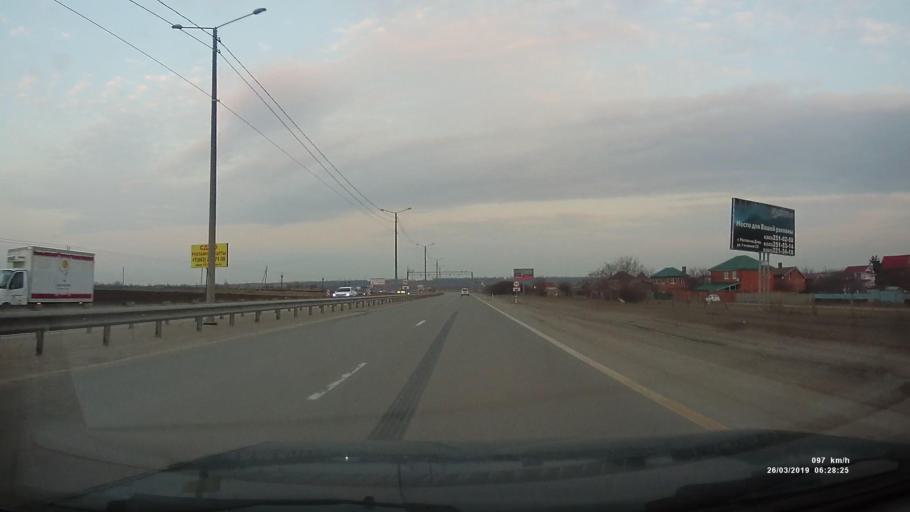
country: RU
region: Rostov
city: Krym
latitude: 47.2655
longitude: 39.5935
